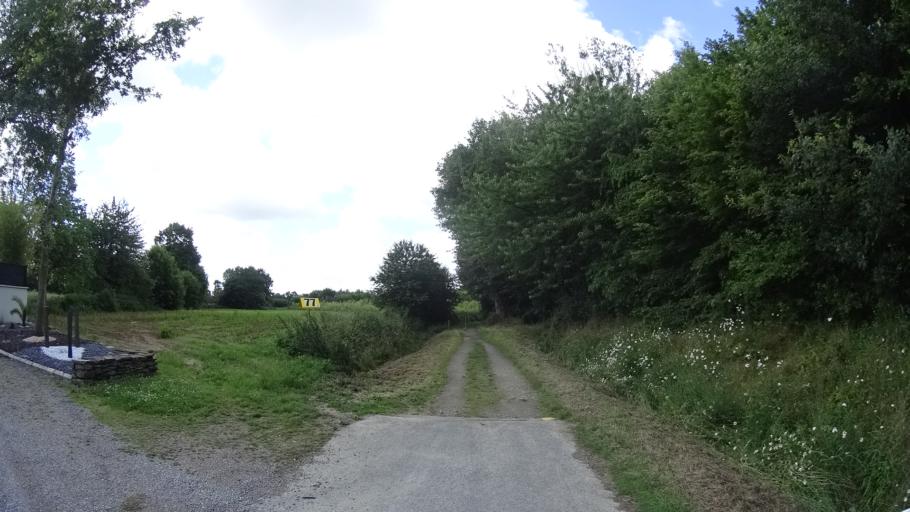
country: FR
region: Brittany
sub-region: Departement d'Ille-et-Vilaine
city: Le Rheu
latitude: 48.1192
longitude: -1.8100
